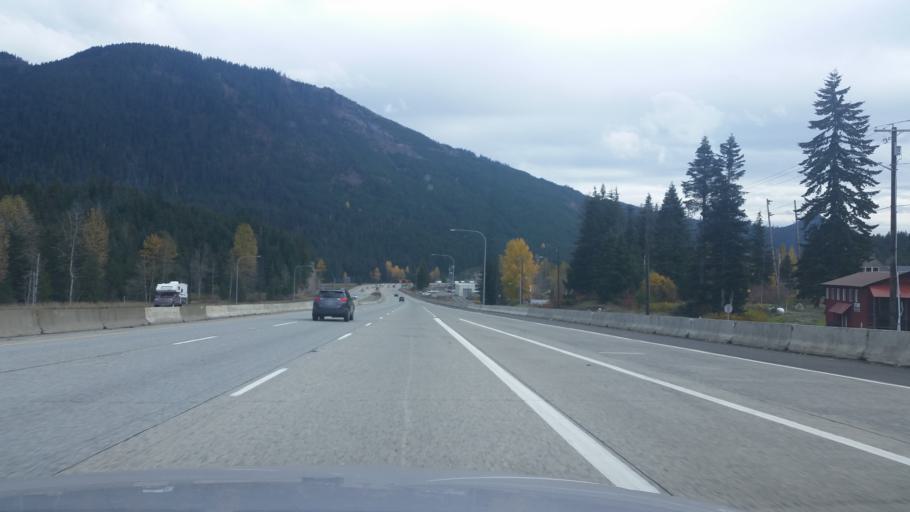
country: US
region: Washington
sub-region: King County
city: Tanner
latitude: 47.3948
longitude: -121.3944
